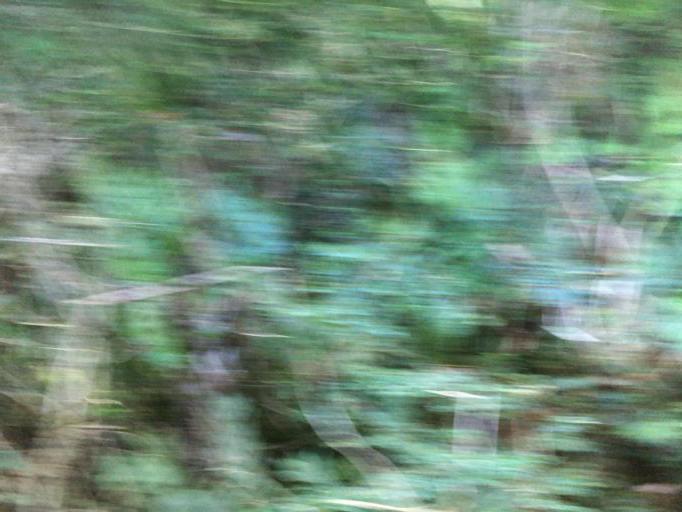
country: TW
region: Taiwan
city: Daxi
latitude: 24.5730
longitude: 121.4190
